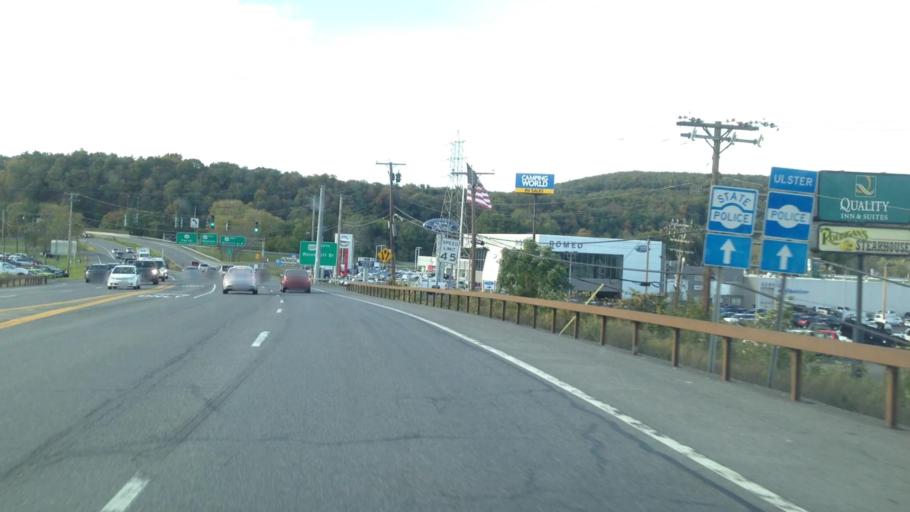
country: US
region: New York
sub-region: Ulster County
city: Lincoln Park
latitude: 41.9464
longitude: -74.0309
